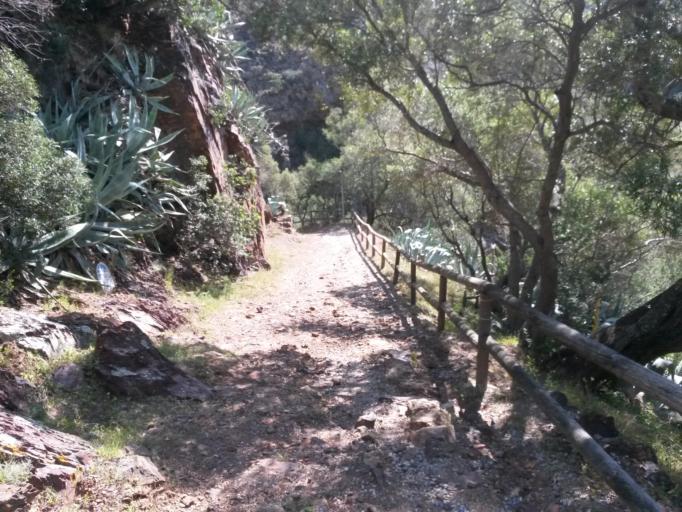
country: IT
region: Tuscany
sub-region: Provincia di Livorno
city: Porto Azzurro
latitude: 42.7840
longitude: 10.3920
